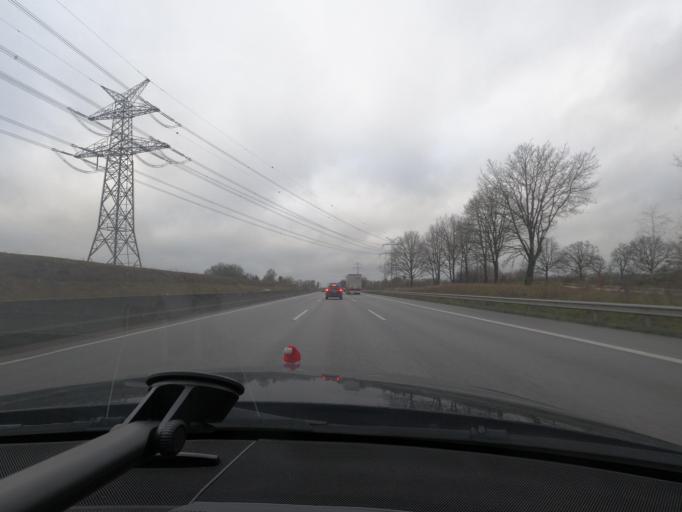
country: DE
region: Schleswig-Holstein
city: Alveslohe
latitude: 53.7919
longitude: 9.9355
